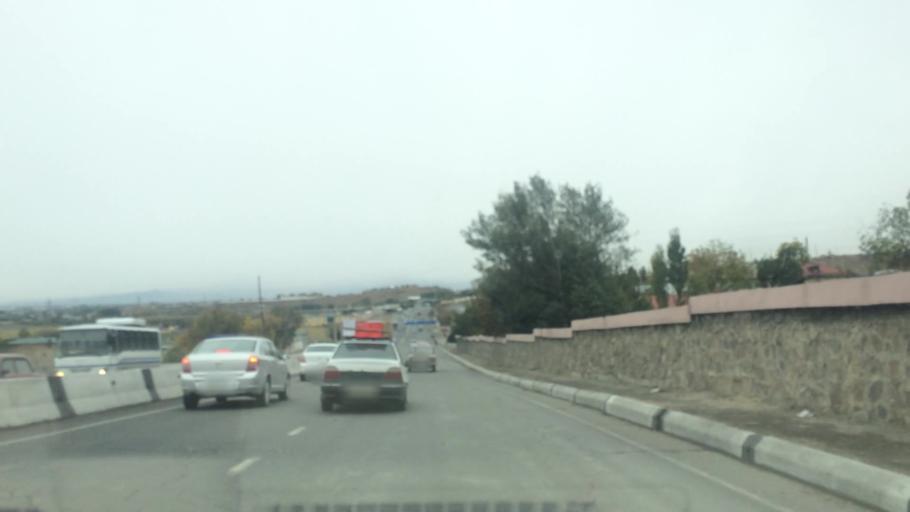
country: UZ
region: Samarqand
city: Jomboy
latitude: 39.6831
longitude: 67.0510
